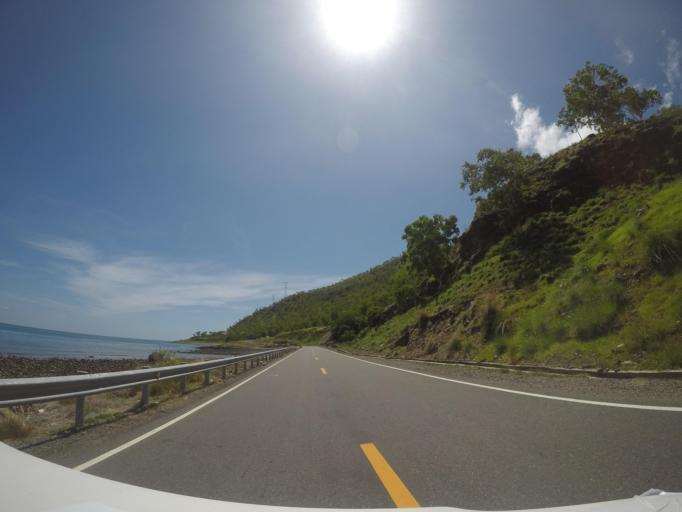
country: TL
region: Manatuto
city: Manatuto
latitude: -8.4787
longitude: 125.9337
